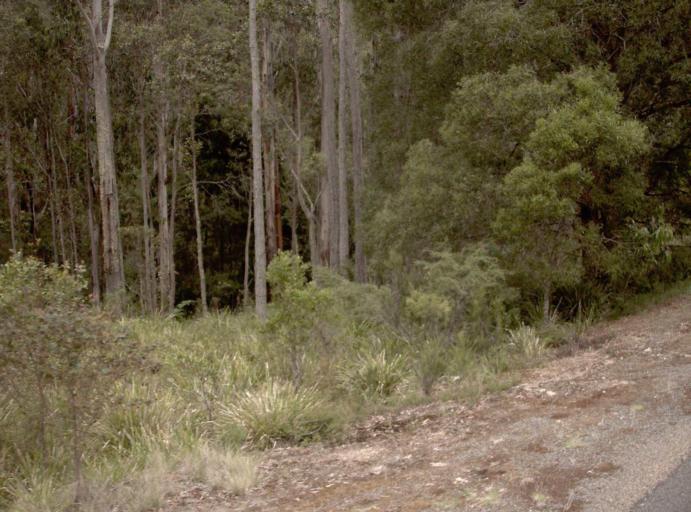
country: AU
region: New South Wales
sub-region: Bombala
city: Bombala
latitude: -37.2326
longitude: 149.2718
